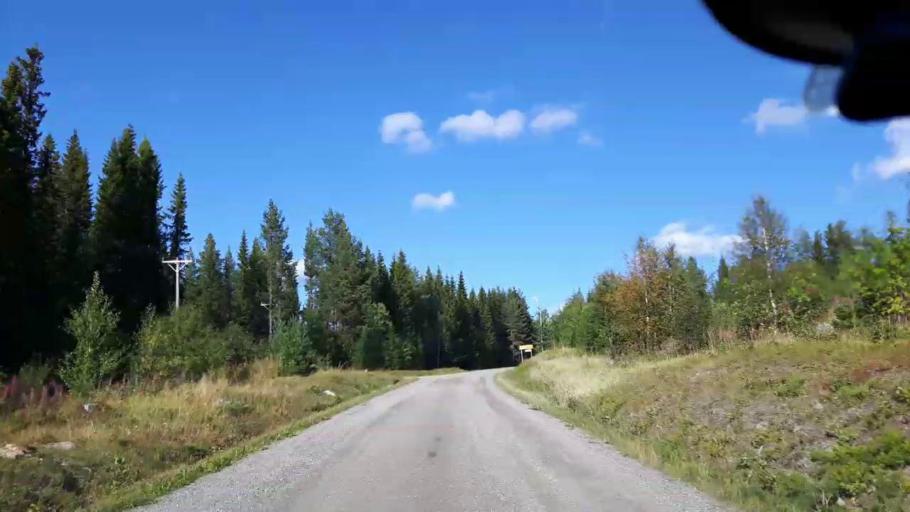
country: SE
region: Jaemtland
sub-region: Ragunda Kommun
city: Hammarstrand
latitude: 63.4402
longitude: 15.9492
